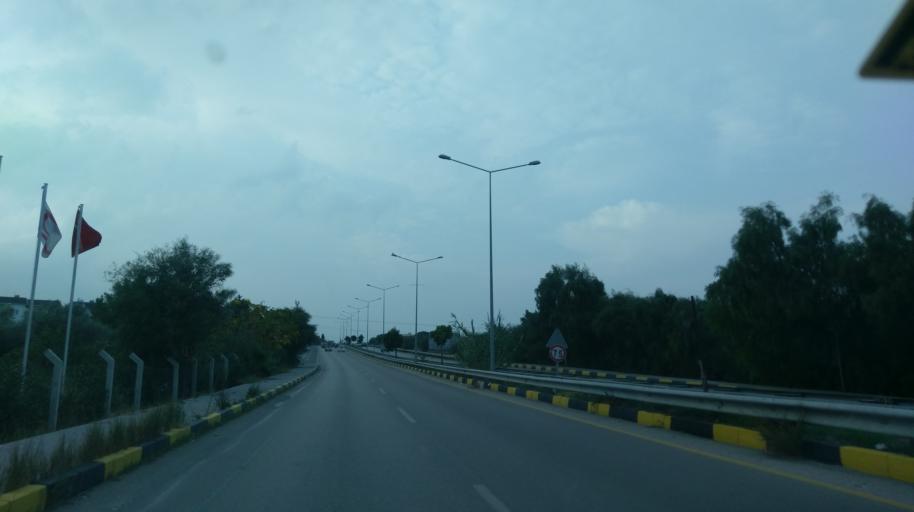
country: CY
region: Keryneia
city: Kyrenia
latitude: 35.3351
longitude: 33.2614
